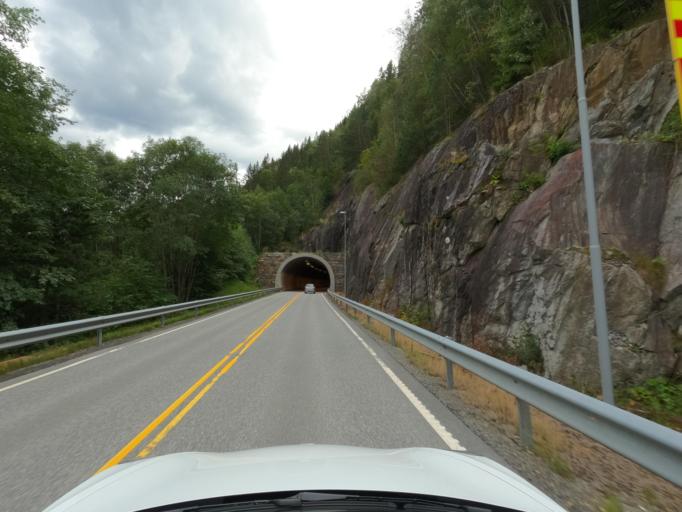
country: NO
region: Telemark
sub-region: Hjartdal
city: Sauland
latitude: 59.8755
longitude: 8.9174
